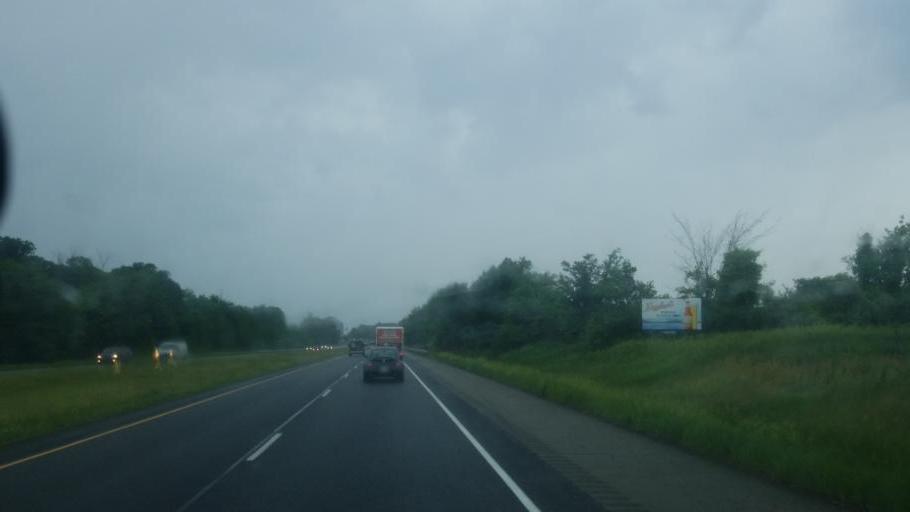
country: US
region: Indiana
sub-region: Whitley County
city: Churubusco
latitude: 41.1264
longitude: -85.3654
